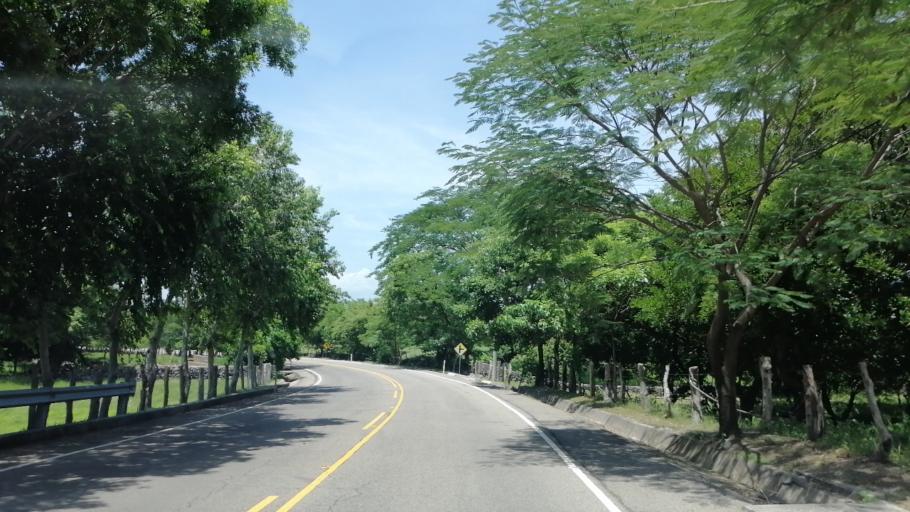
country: SV
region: Chalatenango
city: Nueva Concepcion
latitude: 14.1488
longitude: -89.3057
